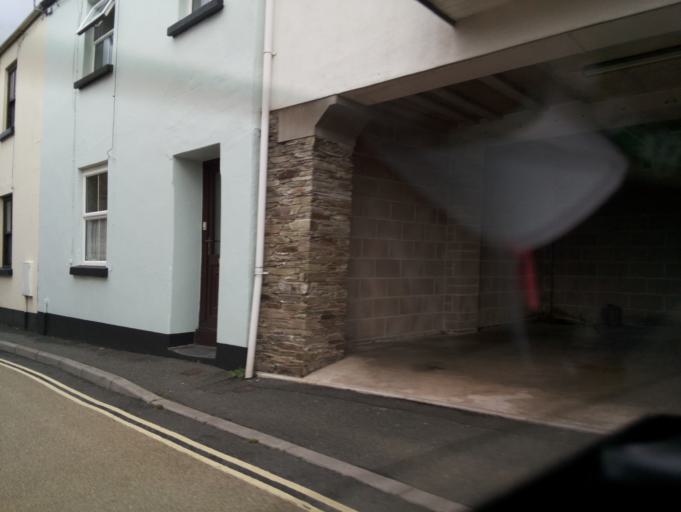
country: GB
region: England
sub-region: Devon
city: Kingsbridge
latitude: 50.2866
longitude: -3.7746
